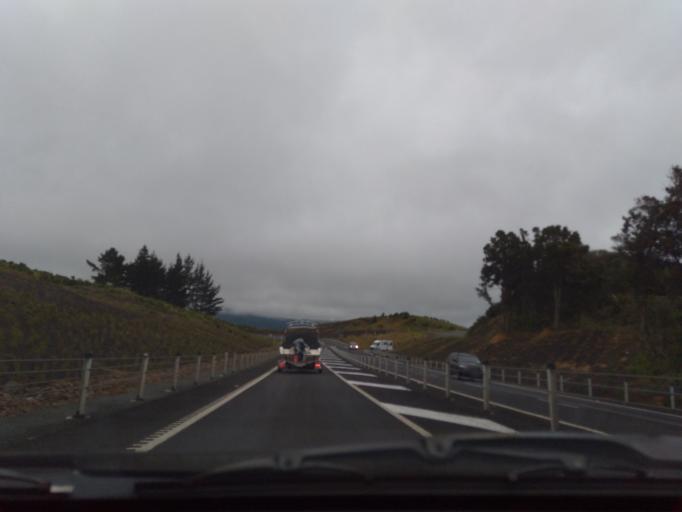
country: NZ
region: Northland
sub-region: Whangarei
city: Ruakaka
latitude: -36.0565
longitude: 174.4259
